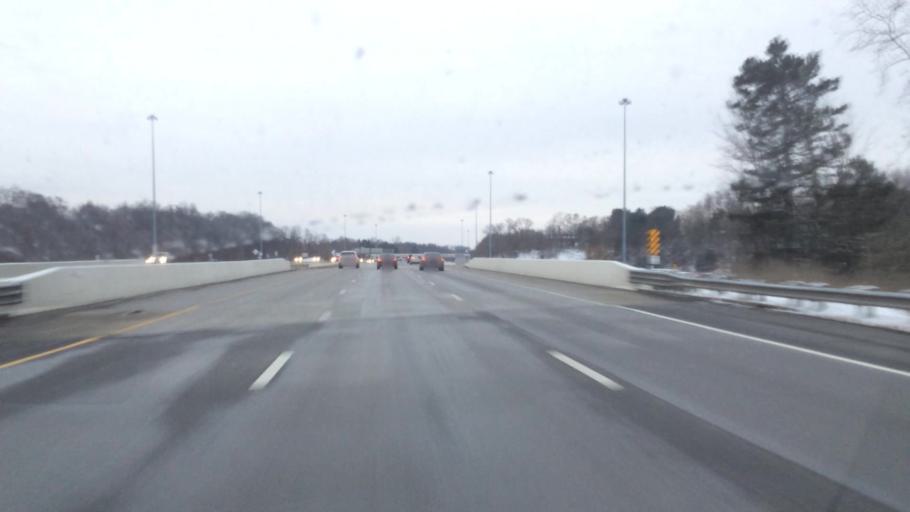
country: US
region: Ohio
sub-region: Medina County
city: Medina
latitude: 41.1624
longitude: -81.7855
